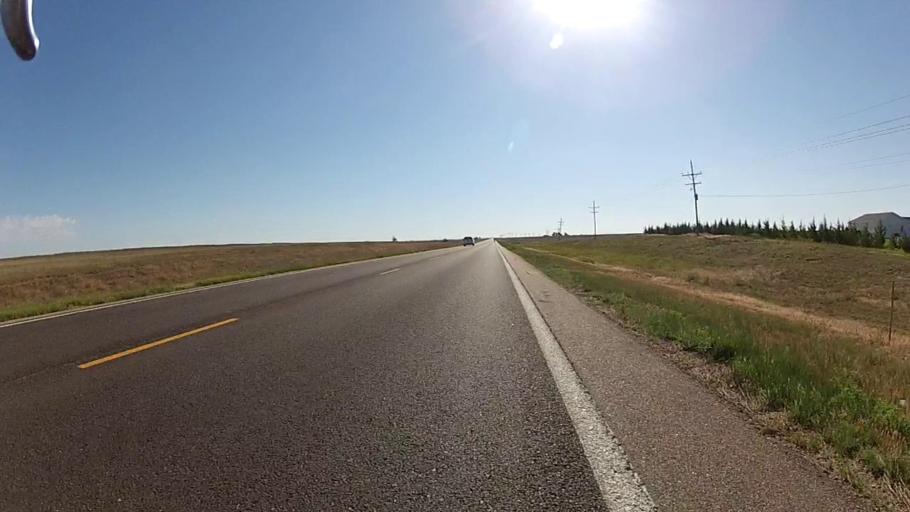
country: US
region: Kansas
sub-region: Haskell County
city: Sublette
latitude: 37.5471
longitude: -100.6135
